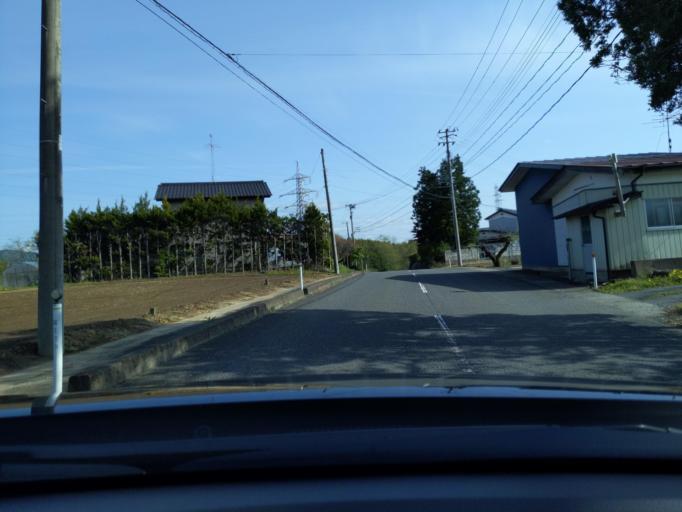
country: JP
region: Fukushima
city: Sukagawa
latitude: 37.3105
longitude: 140.4189
